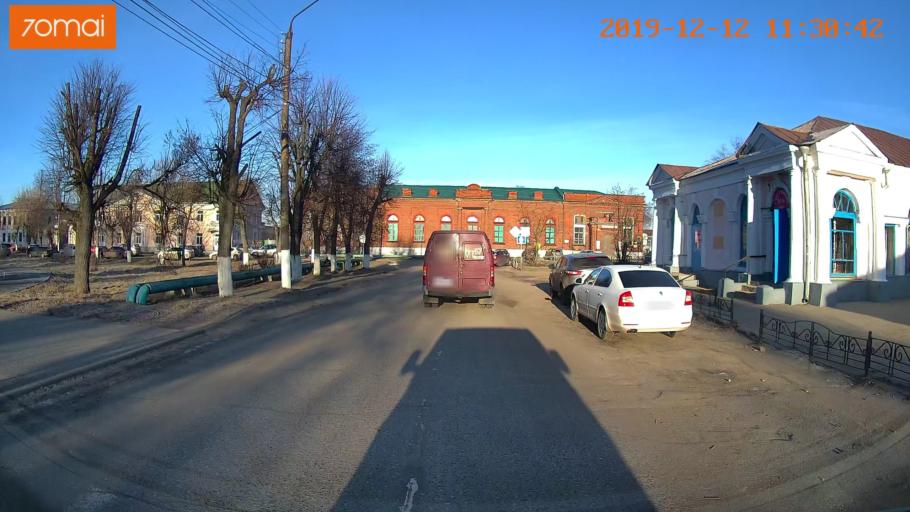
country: RU
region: Ivanovo
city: Shuya
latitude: 56.8550
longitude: 41.3785
